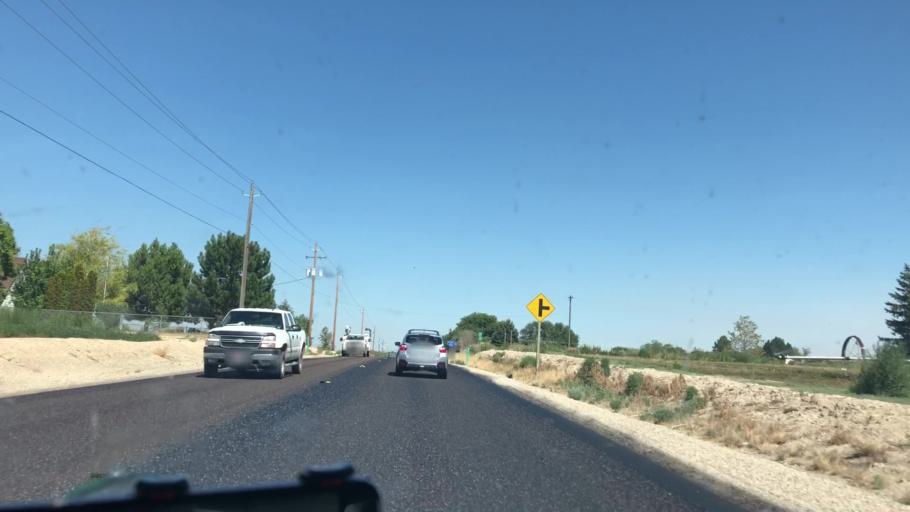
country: US
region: Idaho
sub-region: Canyon County
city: Caldwell
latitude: 43.6037
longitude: -116.7262
